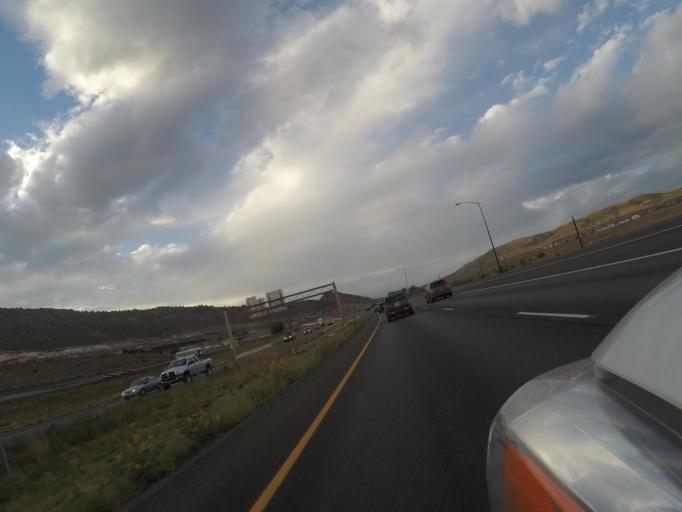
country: US
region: Colorado
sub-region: Jefferson County
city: Indian Hills
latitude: 39.6579
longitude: -105.1820
